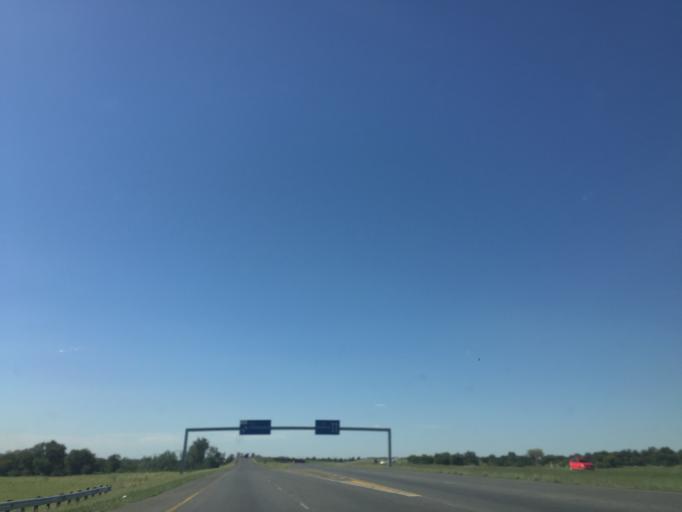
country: ZA
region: Gauteng
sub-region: Sedibeng District Municipality
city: Vereeniging
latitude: -26.6856
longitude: 27.9052
